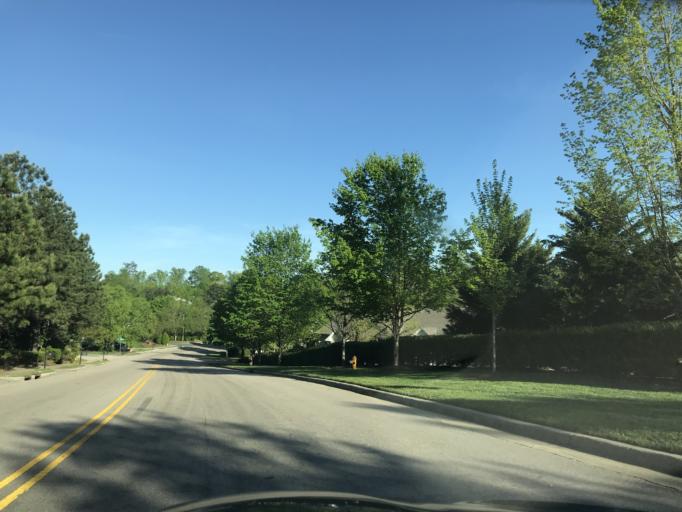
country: US
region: North Carolina
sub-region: Wake County
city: Knightdale
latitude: 35.8393
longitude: -78.5651
